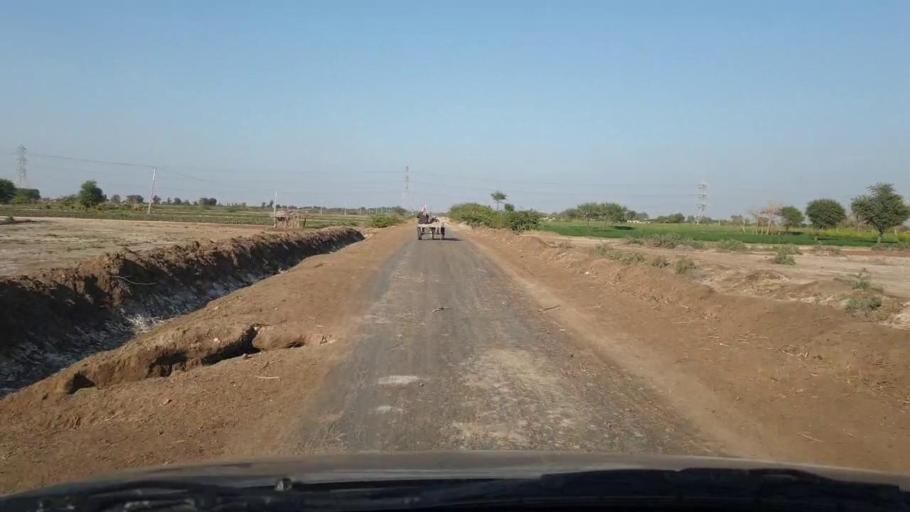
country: PK
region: Sindh
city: Samaro
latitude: 25.1477
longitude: 69.3075
